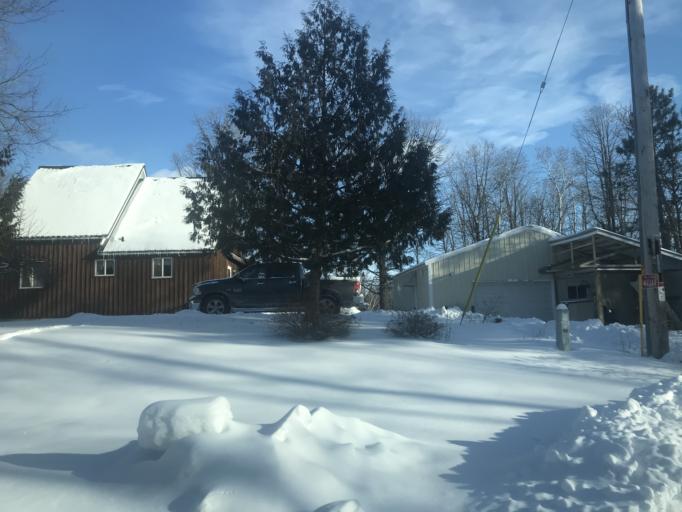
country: US
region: Michigan
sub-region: Menominee County
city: Menominee
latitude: 45.2939
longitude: -87.6939
